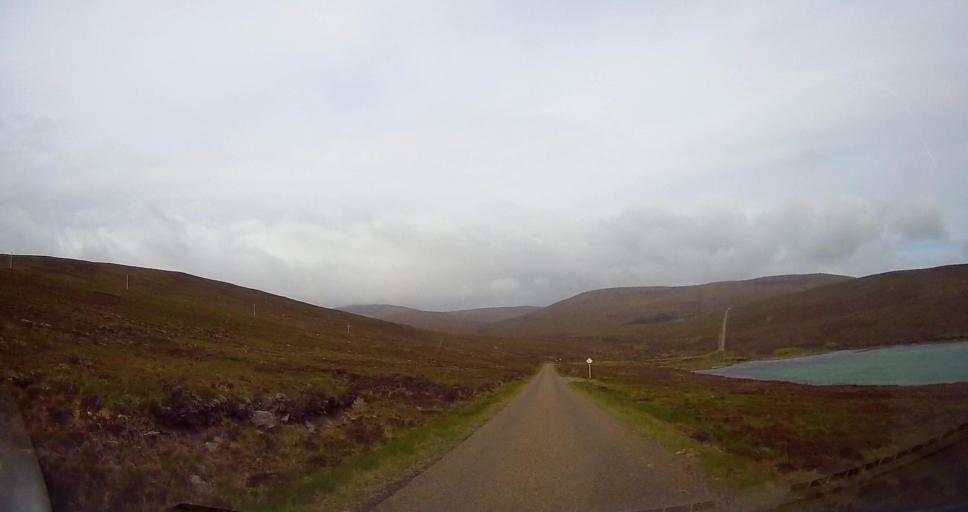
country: GB
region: Scotland
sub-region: Orkney Islands
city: Stromness
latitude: 58.8676
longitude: -3.2228
